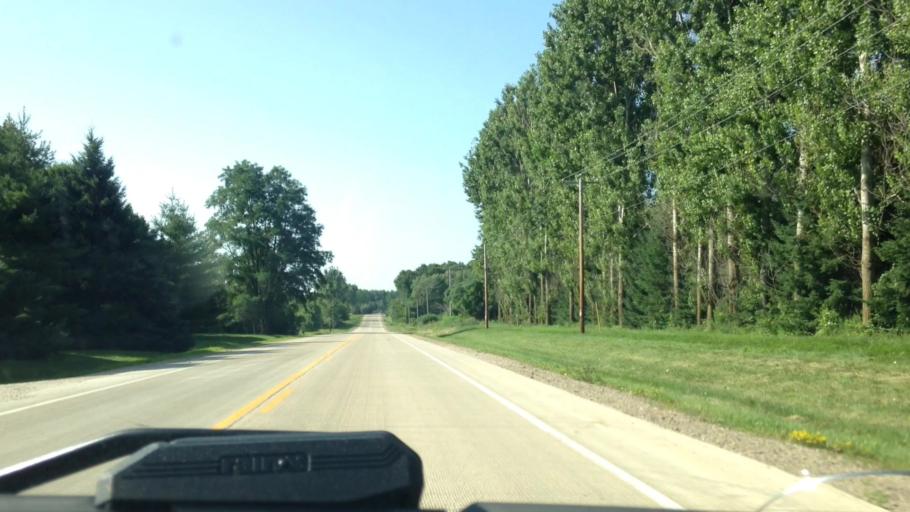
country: US
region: Wisconsin
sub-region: Dodge County
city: Mayville
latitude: 43.4635
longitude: -88.5614
